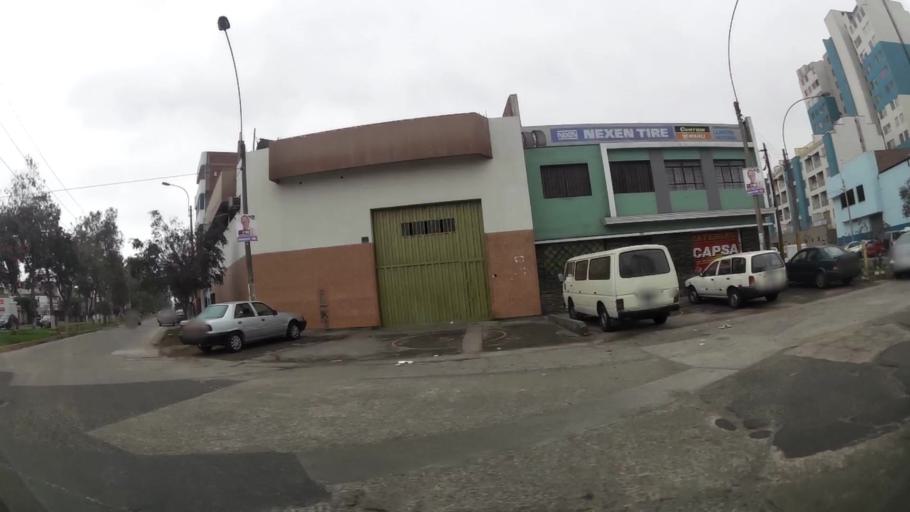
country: PE
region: Lima
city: Lima
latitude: -12.0665
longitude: -77.0543
